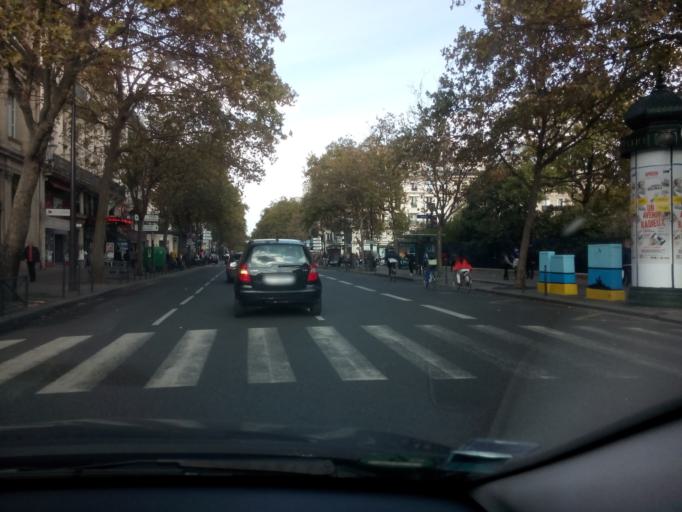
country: FR
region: Ile-de-France
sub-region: Paris
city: Paris
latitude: 48.8578
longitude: 2.3478
